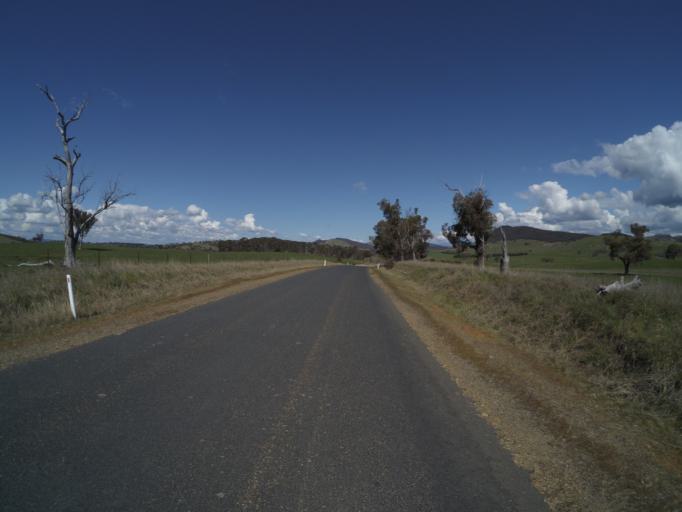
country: AU
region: New South Wales
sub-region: Yass Valley
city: Murrumbateman
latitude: -35.1241
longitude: 148.8685
